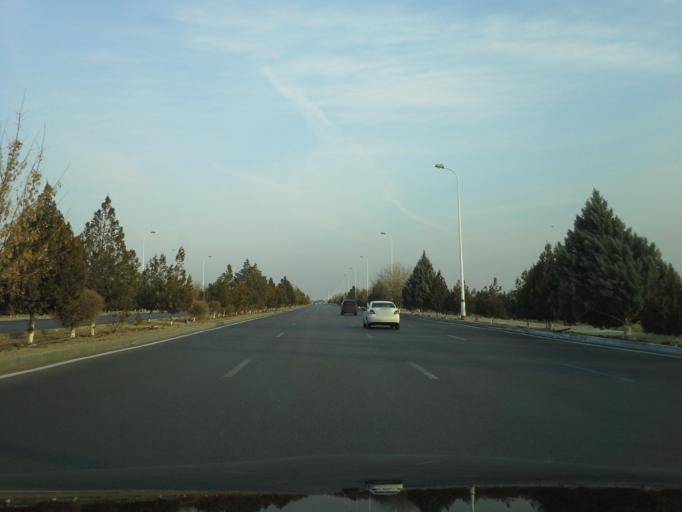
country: TM
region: Ahal
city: Abadan
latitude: 38.0389
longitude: 58.2142
